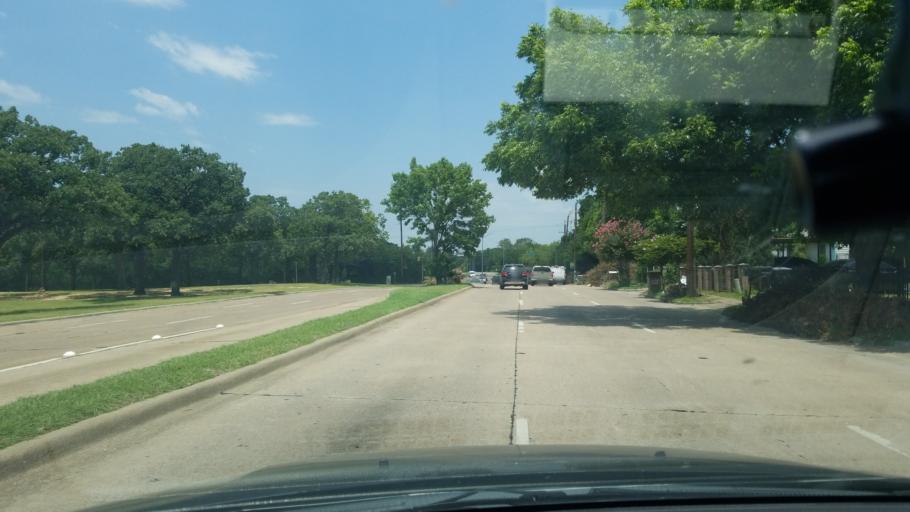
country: US
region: Texas
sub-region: Dallas County
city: Balch Springs
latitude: 32.7181
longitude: -96.6655
